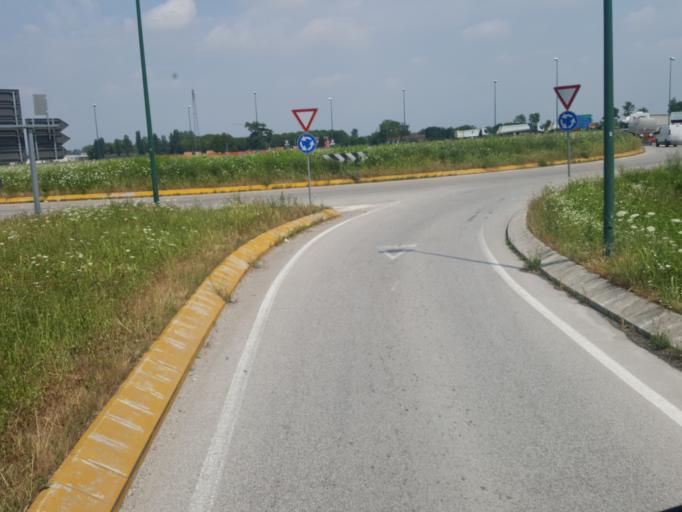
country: IT
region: Veneto
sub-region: Provincia di Treviso
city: Lancenigo-Villorba
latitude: 45.7394
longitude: 12.2586
